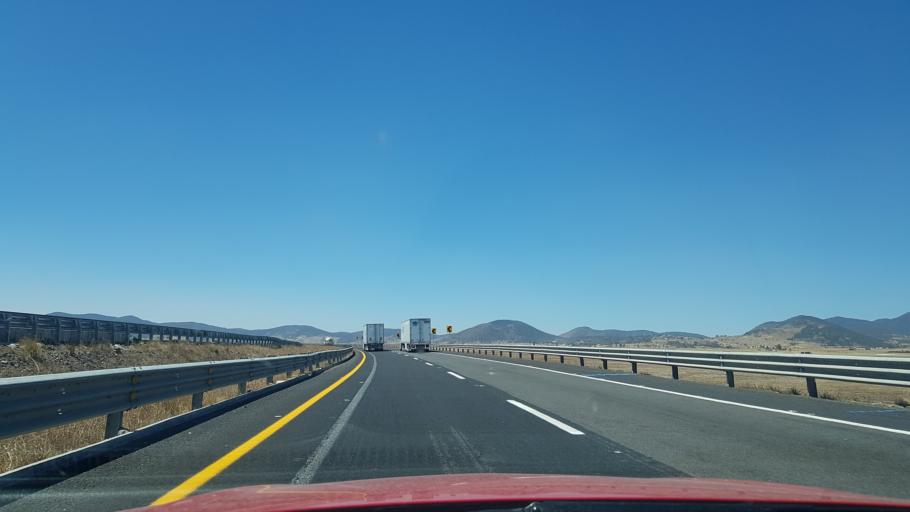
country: MX
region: Mexico
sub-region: Timilpan
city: Tercera Manzana de Zaragoza
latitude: 19.9572
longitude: -99.7016
